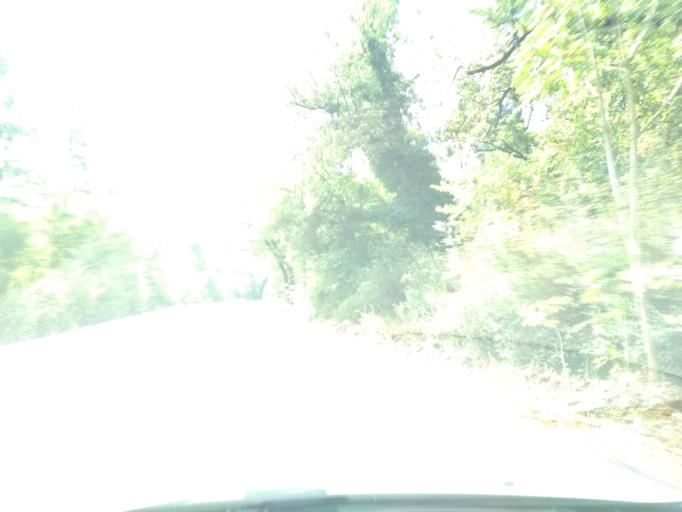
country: GR
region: Central Greece
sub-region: Nomos Evvoias
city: Prokopion
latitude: 38.7285
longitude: 23.5027
